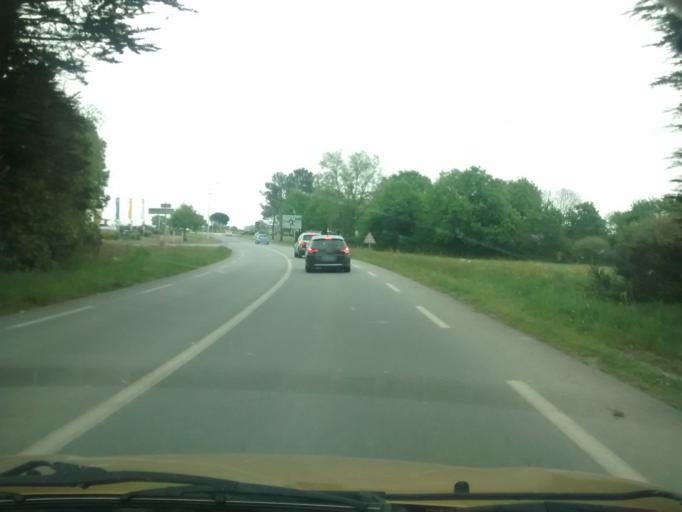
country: FR
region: Brittany
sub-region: Departement du Morbihan
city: Muzillac
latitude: 47.5561
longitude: -2.5124
